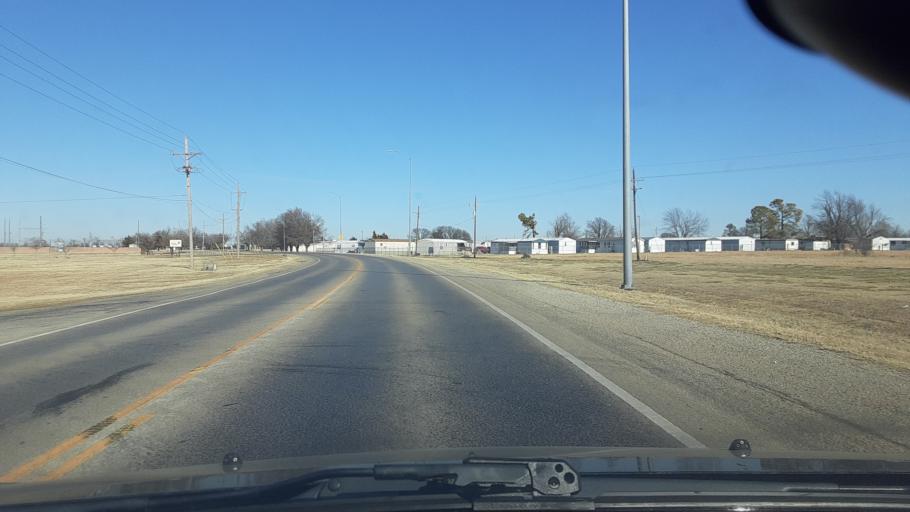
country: US
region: Oklahoma
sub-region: Kay County
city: Ponca City
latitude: 36.7346
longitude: -97.0903
